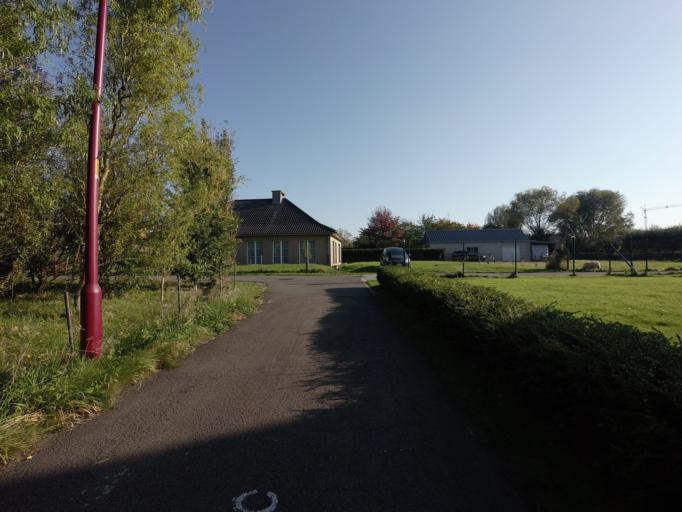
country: BE
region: Flanders
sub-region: Provincie Antwerpen
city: Lint
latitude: 51.1251
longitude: 4.5019
